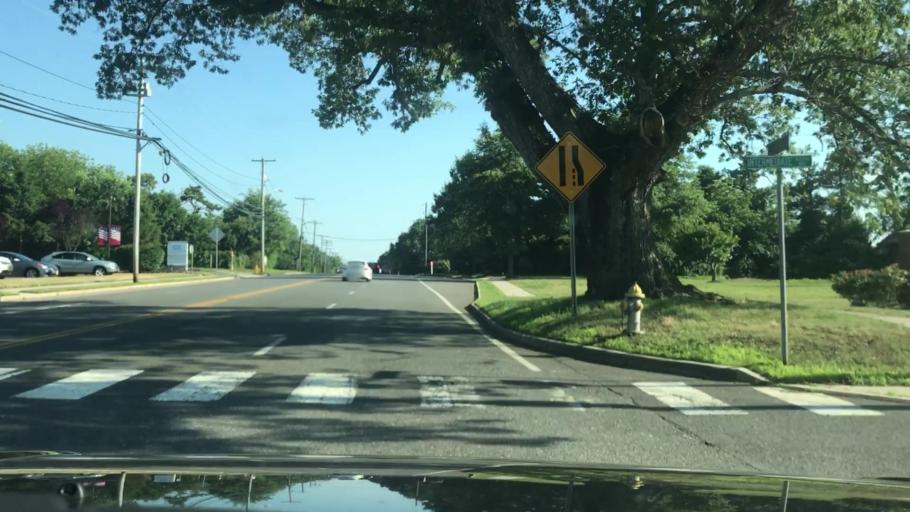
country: US
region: New Jersey
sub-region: Ocean County
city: Toms River
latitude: 39.9904
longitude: -74.1967
